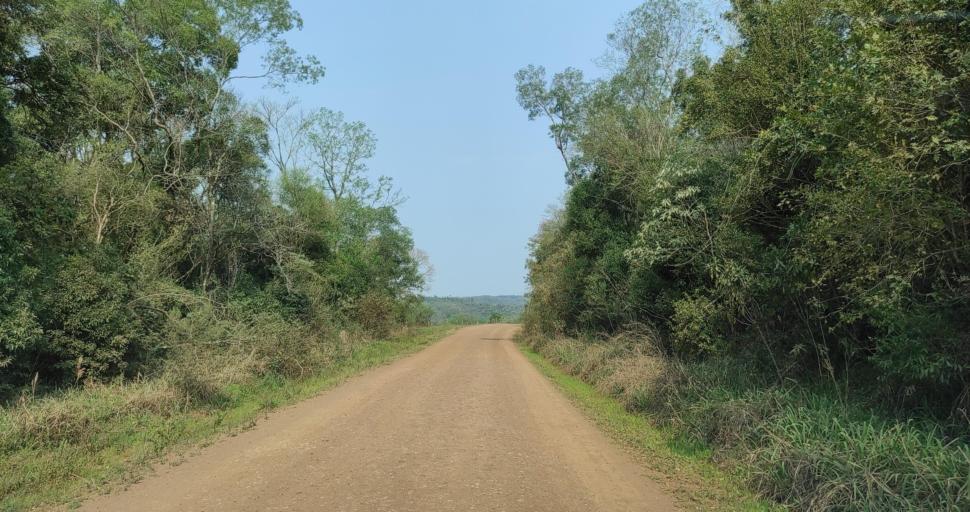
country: AR
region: Misiones
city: Cerro Cora
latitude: -27.5473
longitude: -55.5829
